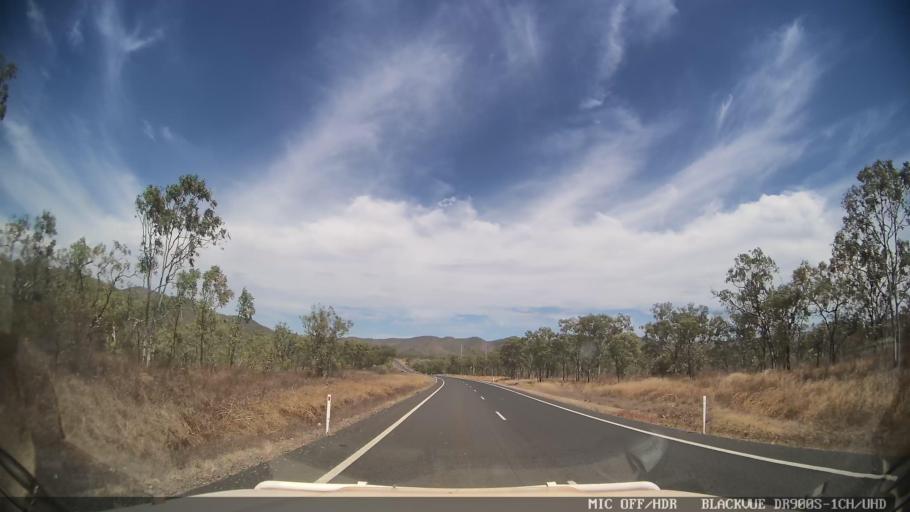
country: AU
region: Queensland
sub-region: Cook
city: Cooktown
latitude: -15.9342
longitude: 144.8393
